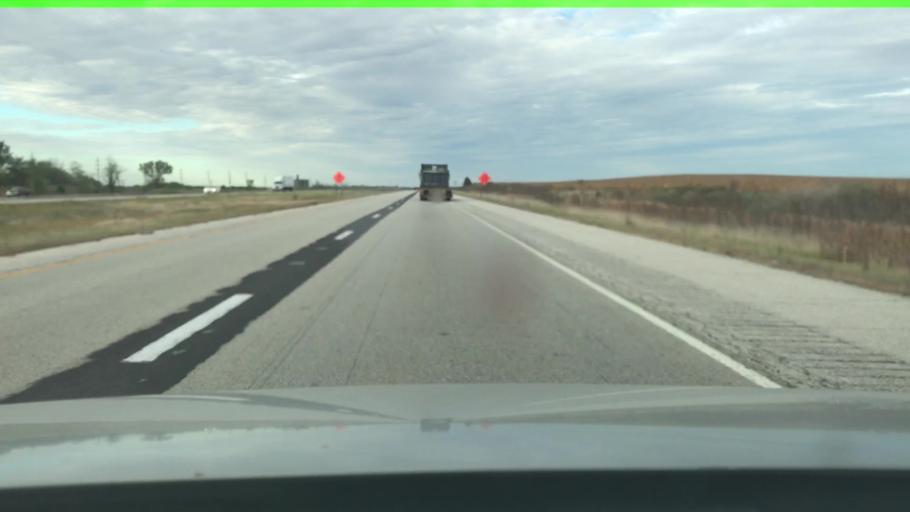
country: US
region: Illinois
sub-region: Livingston County
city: Odell
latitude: 40.9673
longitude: -88.5598
